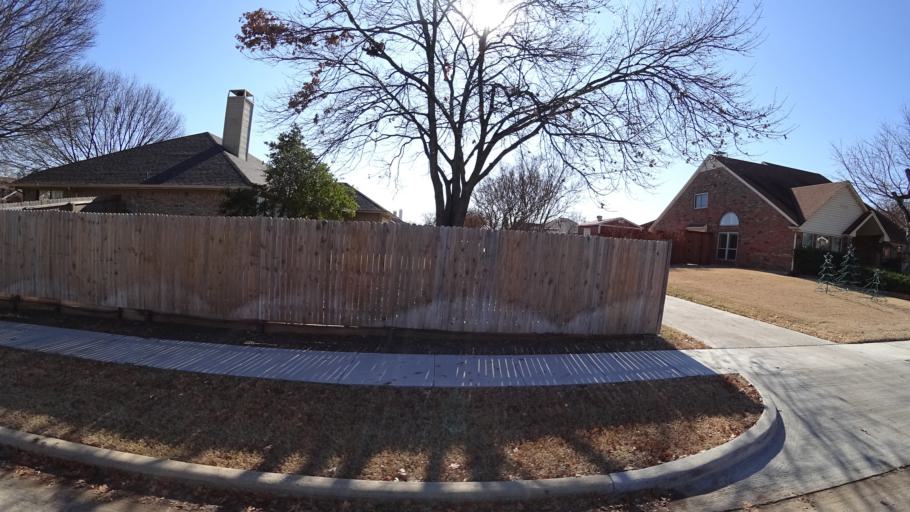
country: US
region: Texas
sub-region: Denton County
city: Lewisville
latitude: 33.0092
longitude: -97.0165
